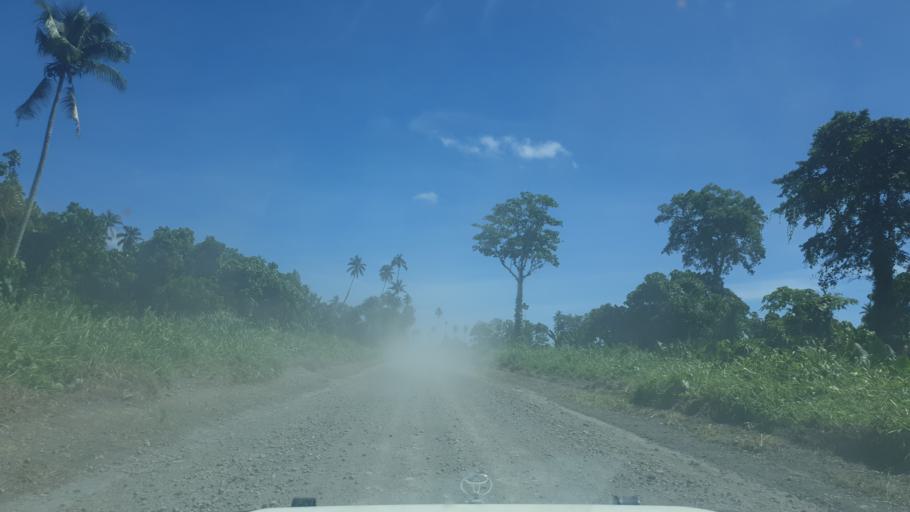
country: PG
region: Bougainville
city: Arawa
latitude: -5.9784
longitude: 155.3512
